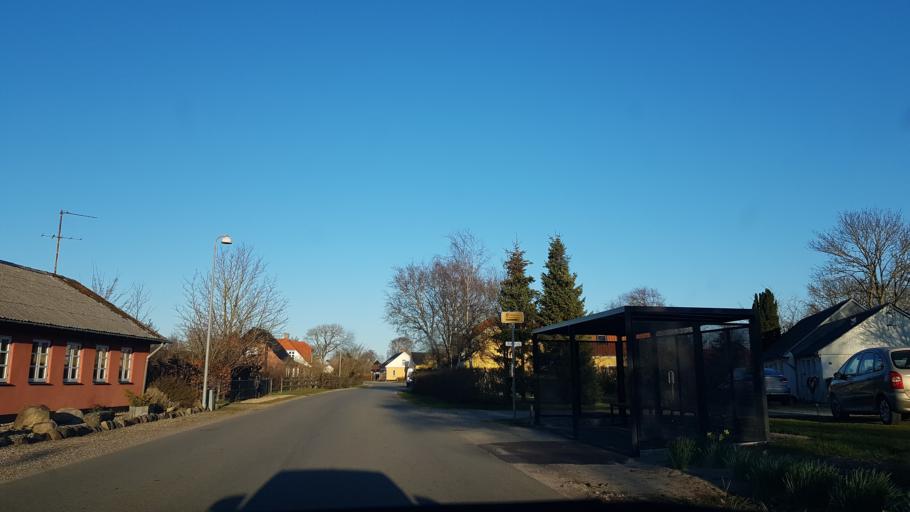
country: DK
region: South Denmark
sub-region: Esbjerg Kommune
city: Bramming
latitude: 55.3975
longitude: 8.7048
